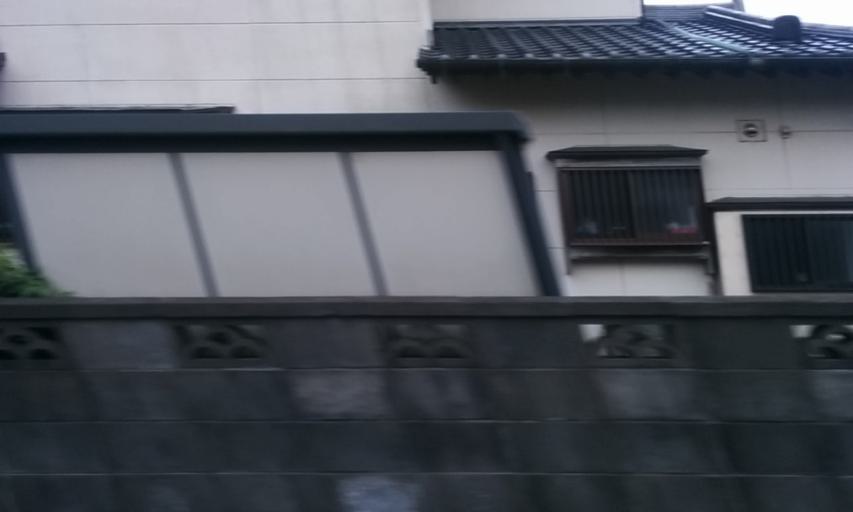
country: JP
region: Chiba
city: Katori-shi
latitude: 35.8929
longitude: 140.5113
